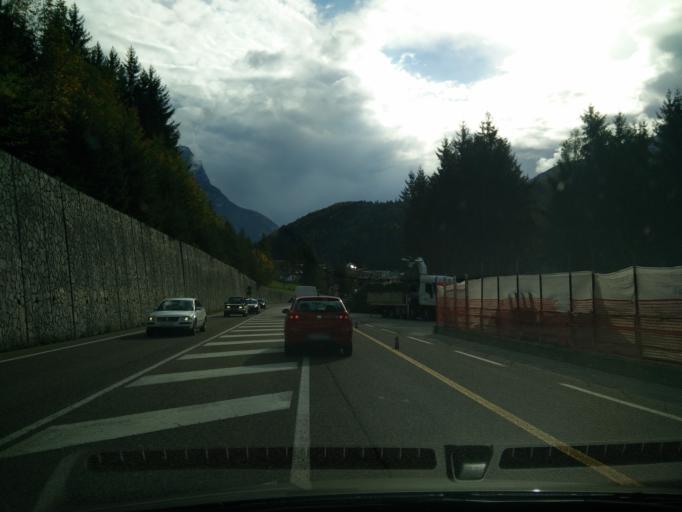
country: IT
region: Veneto
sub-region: Provincia di Belluno
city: Perarolo di Cadore
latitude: 46.3969
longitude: 12.3713
